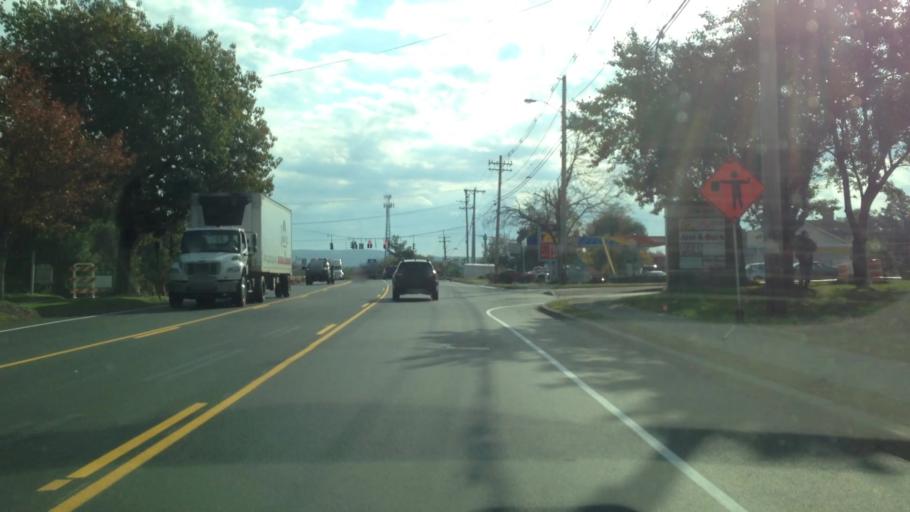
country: US
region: New York
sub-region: Ulster County
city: New Paltz
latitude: 41.7424
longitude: -74.0689
